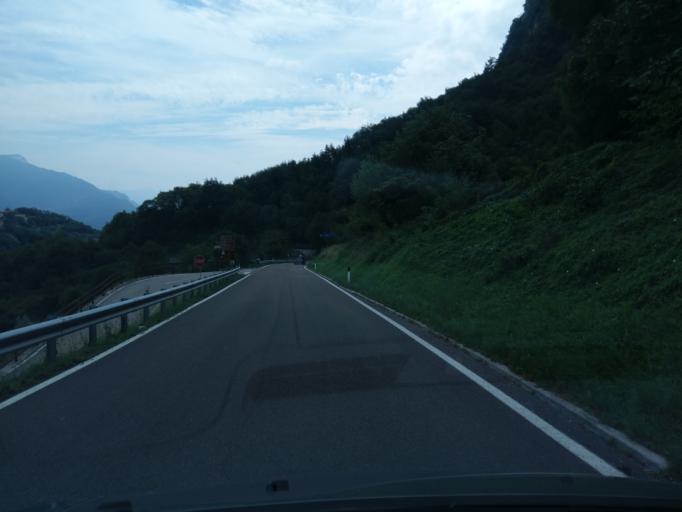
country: IT
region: Trentino-Alto Adige
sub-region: Provincia di Trento
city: Tenno
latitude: 45.9177
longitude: 10.8250
